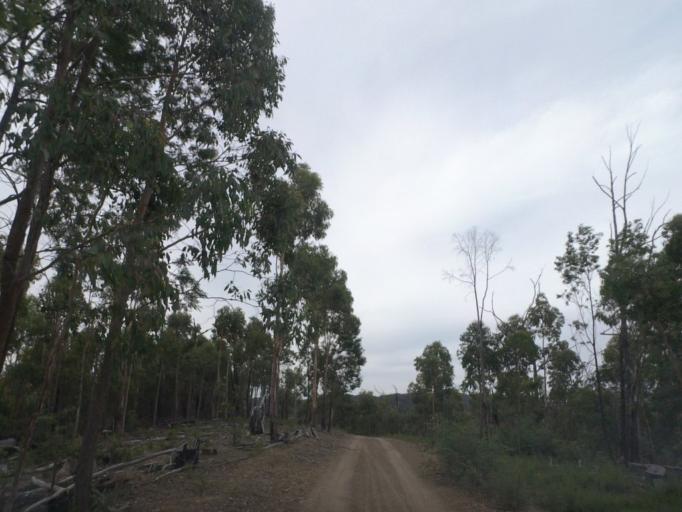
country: AU
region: Victoria
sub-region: Murrindindi
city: Alexandra
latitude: -37.3737
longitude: 145.5577
